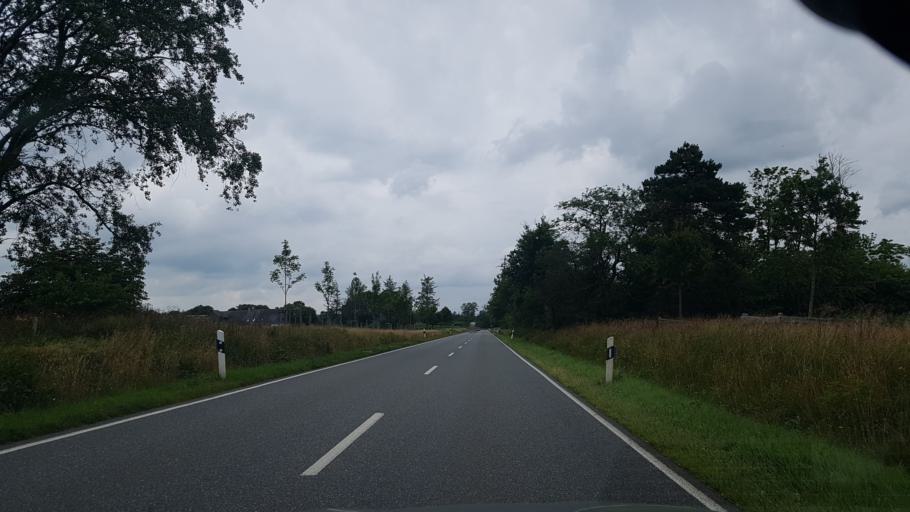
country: DE
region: Schleswig-Holstein
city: Osterby
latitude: 54.8167
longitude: 9.2267
